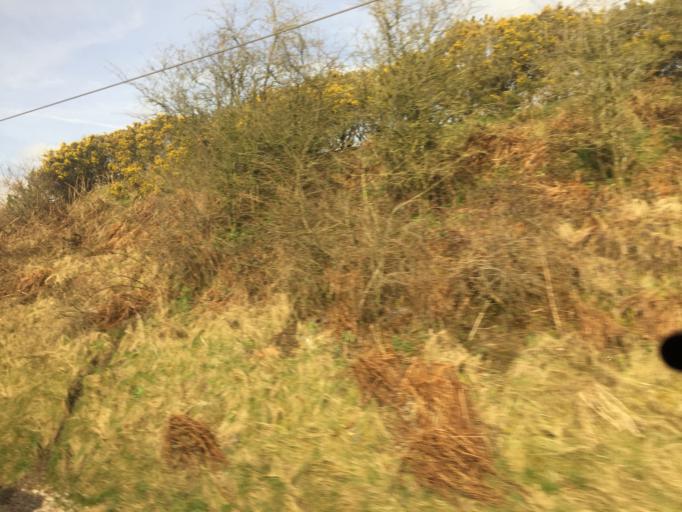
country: GB
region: Scotland
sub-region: Dumfries and Galloway
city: Annan
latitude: 55.0645
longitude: -3.2569
